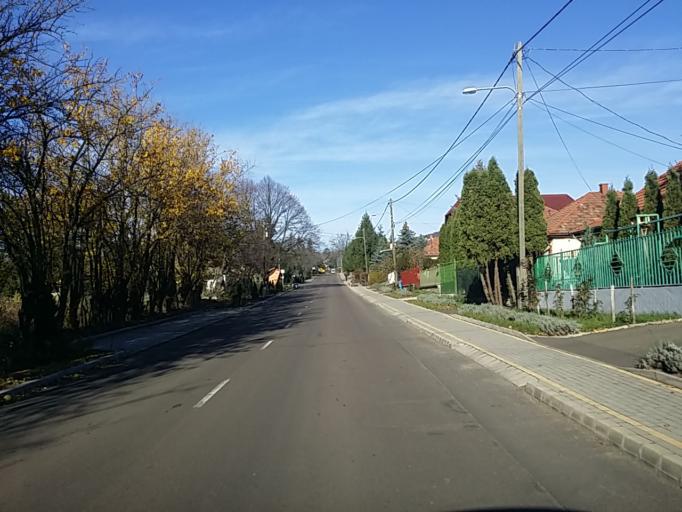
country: HU
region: Heves
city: Abasar
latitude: 47.8113
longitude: 20.0036
